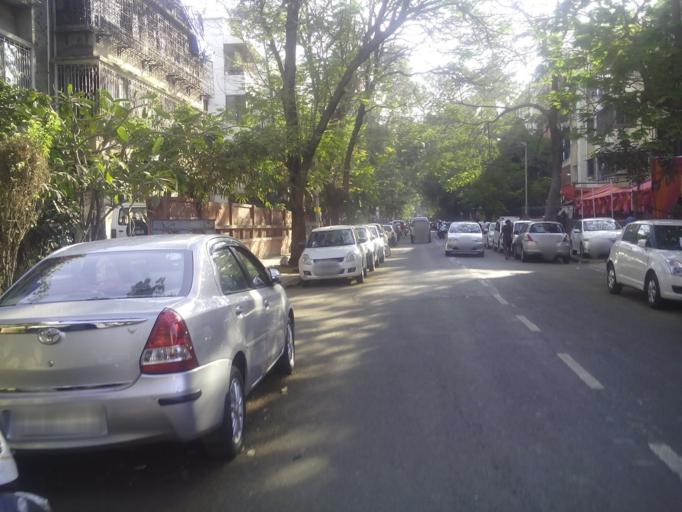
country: IN
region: Maharashtra
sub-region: Mumbai Suburban
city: Mumbai
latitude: 19.0421
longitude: 72.8620
